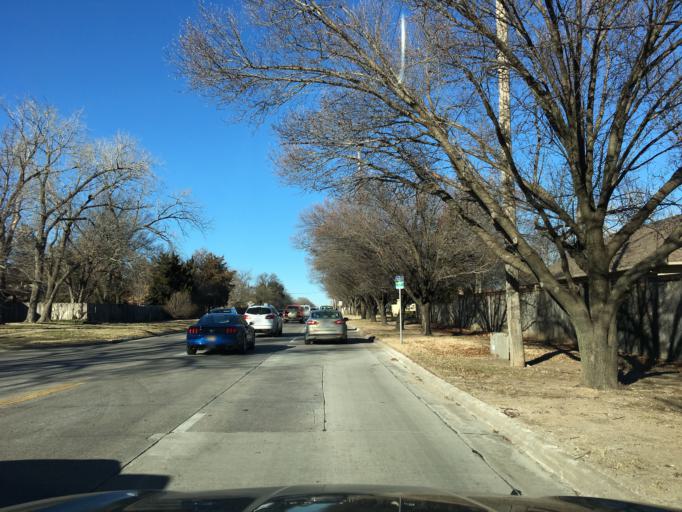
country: US
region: Kansas
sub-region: Sedgwick County
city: Bellaire
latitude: 37.6996
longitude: -97.2446
